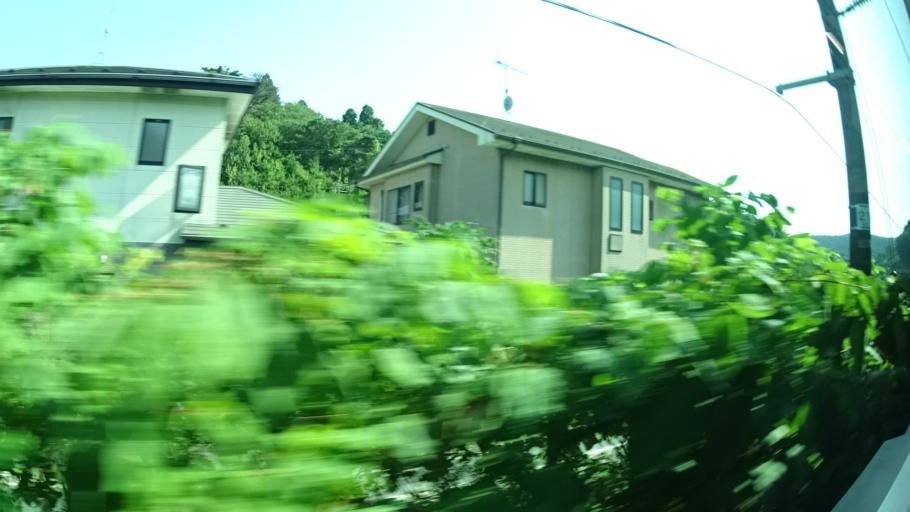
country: JP
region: Miyagi
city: Matsushima
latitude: 38.3778
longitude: 141.0633
